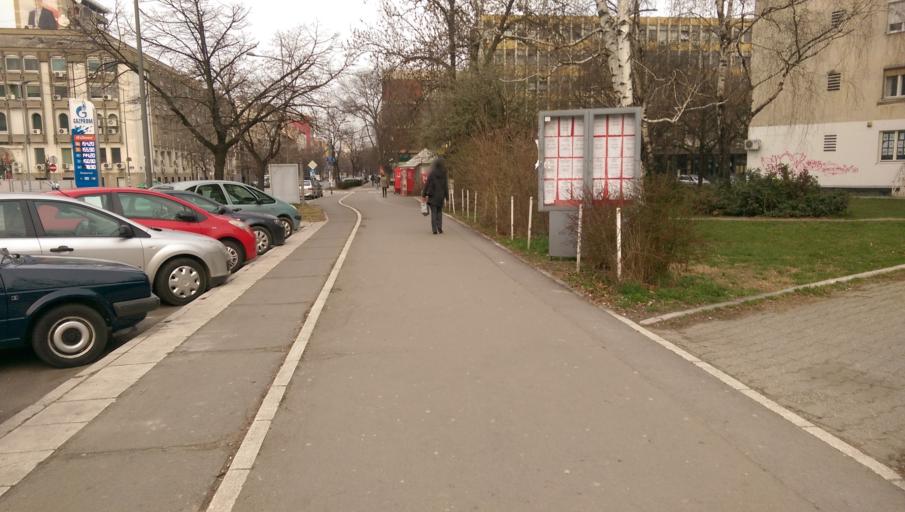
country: RS
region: Autonomna Pokrajina Vojvodina
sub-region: Juznobacki Okrug
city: Novi Sad
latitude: 45.2491
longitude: 19.8444
